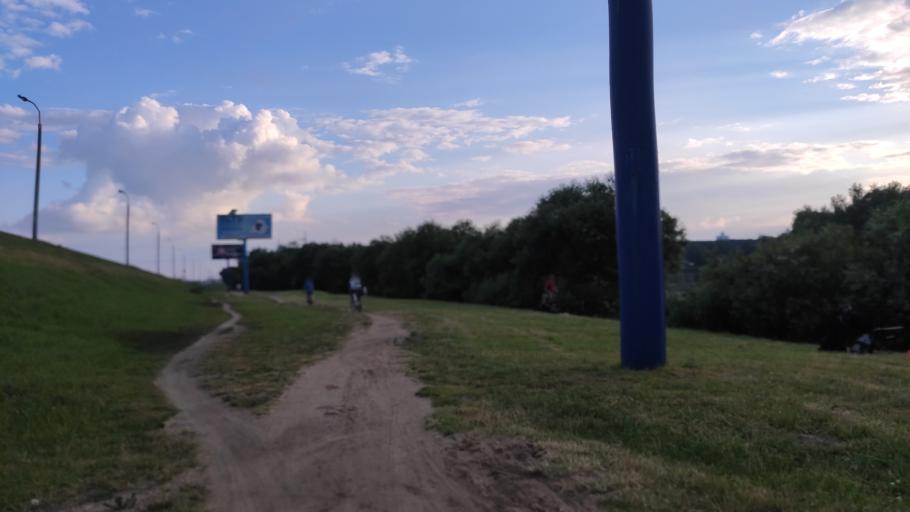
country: BY
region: Minsk
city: Zhdanovichy
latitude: 53.9576
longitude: 27.4536
